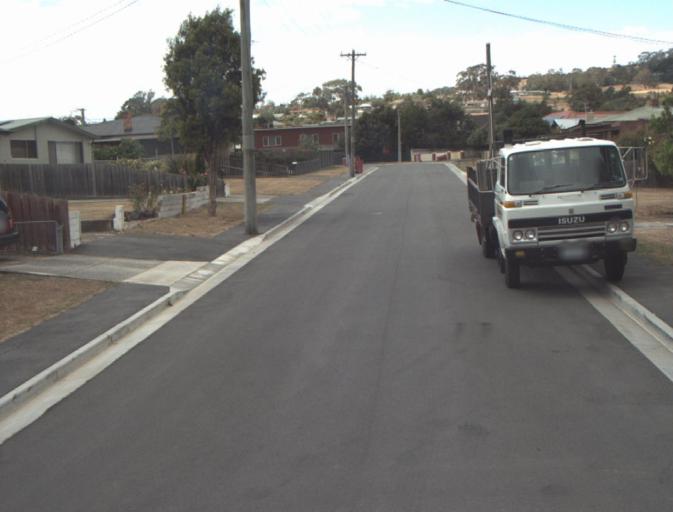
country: AU
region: Tasmania
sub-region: Launceston
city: Newstead
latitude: -41.4556
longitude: 147.1961
